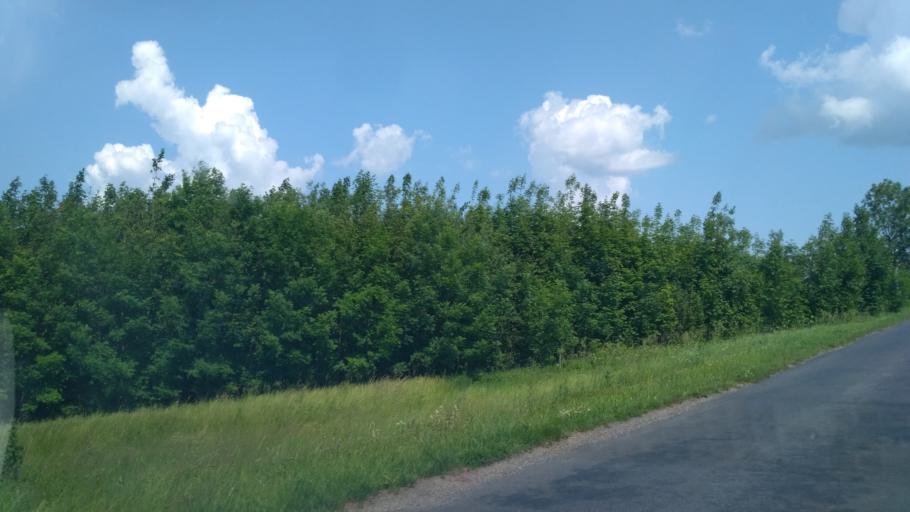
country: PL
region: Subcarpathian Voivodeship
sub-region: Powiat jaroslawski
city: Pruchnik
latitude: 49.9061
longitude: 22.4945
